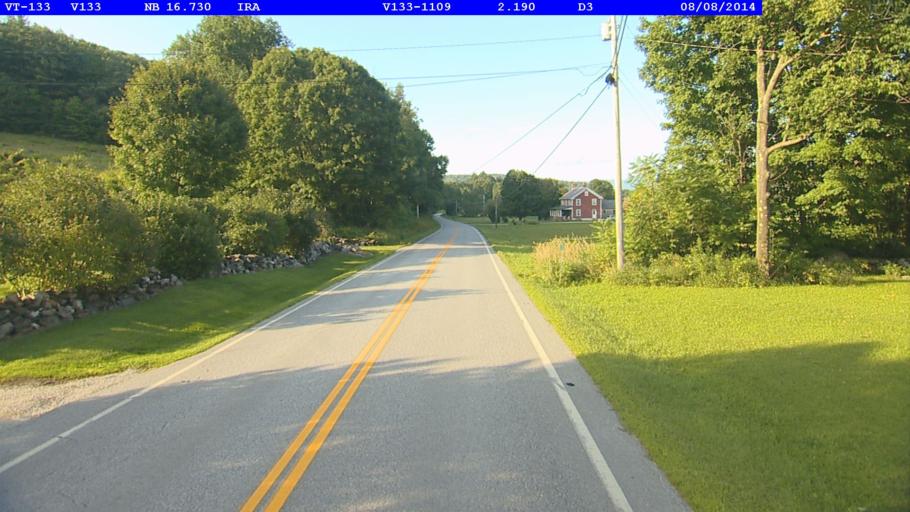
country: US
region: Vermont
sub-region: Rutland County
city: West Rutland
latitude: 43.5252
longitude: -73.0703
